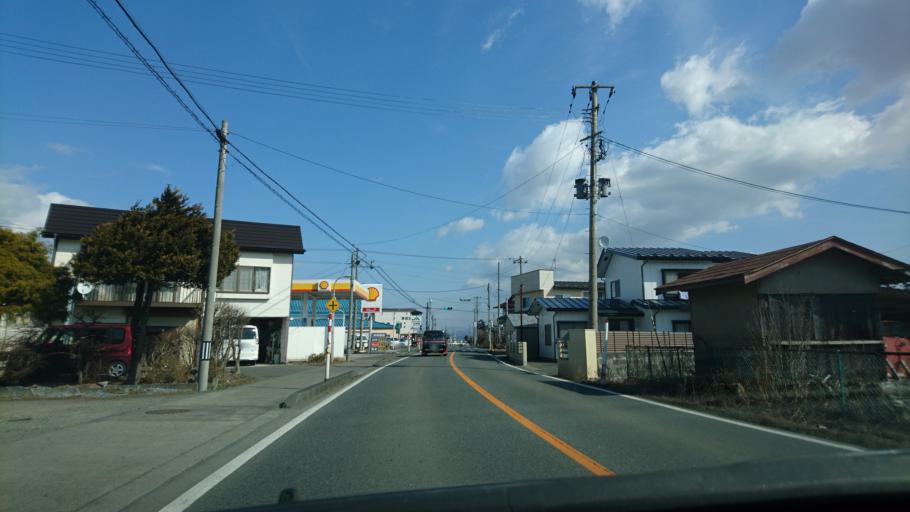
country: JP
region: Iwate
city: Morioka-shi
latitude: 39.5678
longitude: 141.1085
